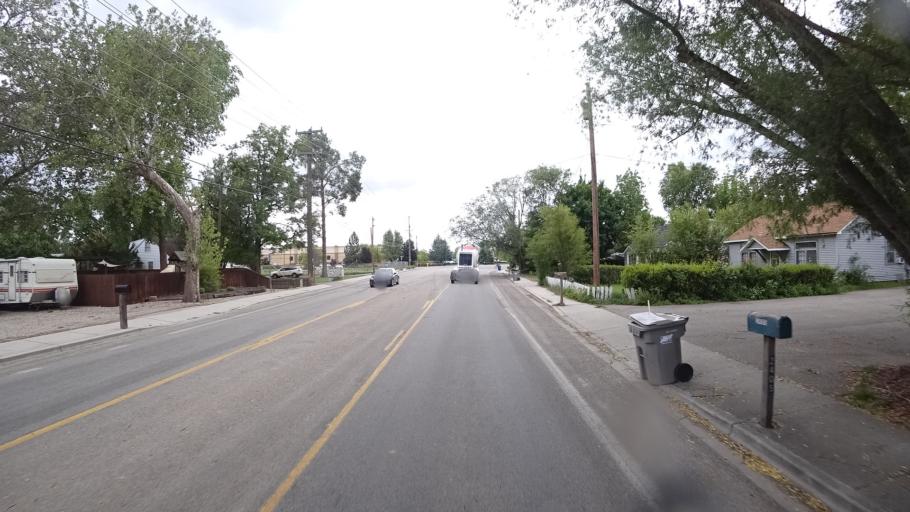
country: US
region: Idaho
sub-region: Ada County
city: Garden City
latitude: 43.6420
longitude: -116.2334
